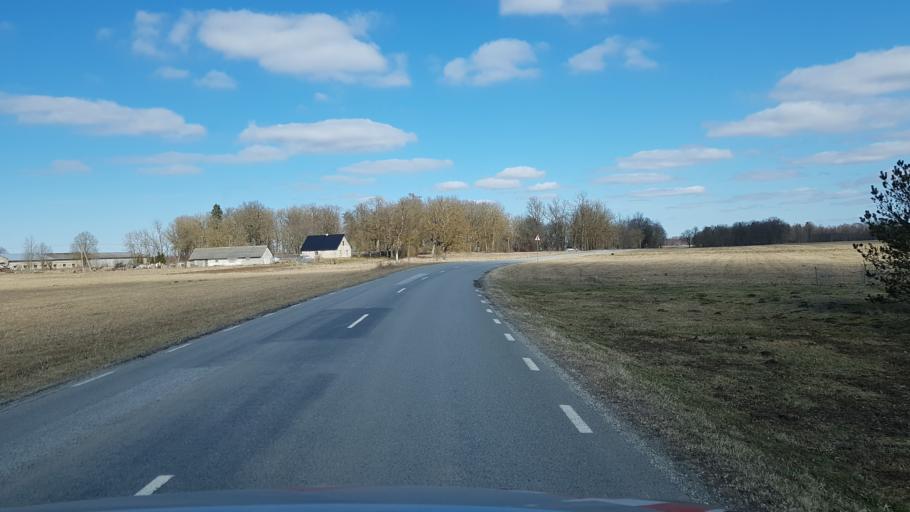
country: EE
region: Laeaene-Virumaa
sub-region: Tapa vald
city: Tapa
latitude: 59.2697
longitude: 25.8565
